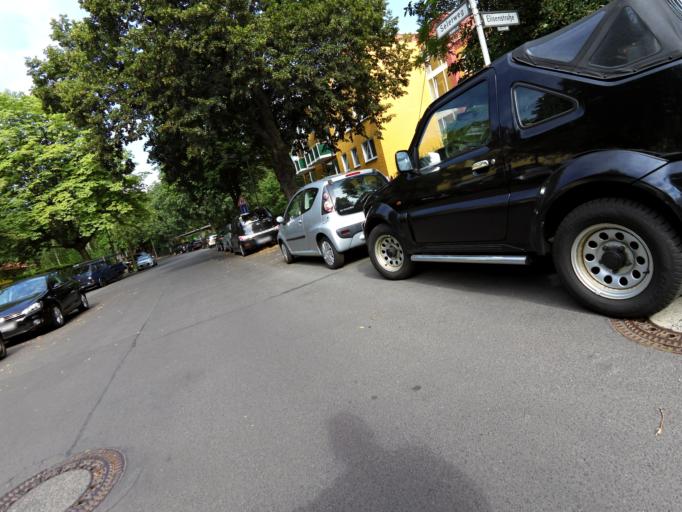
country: DE
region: Berlin
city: Steglitz Bezirk
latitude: 52.4546
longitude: 13.3346
